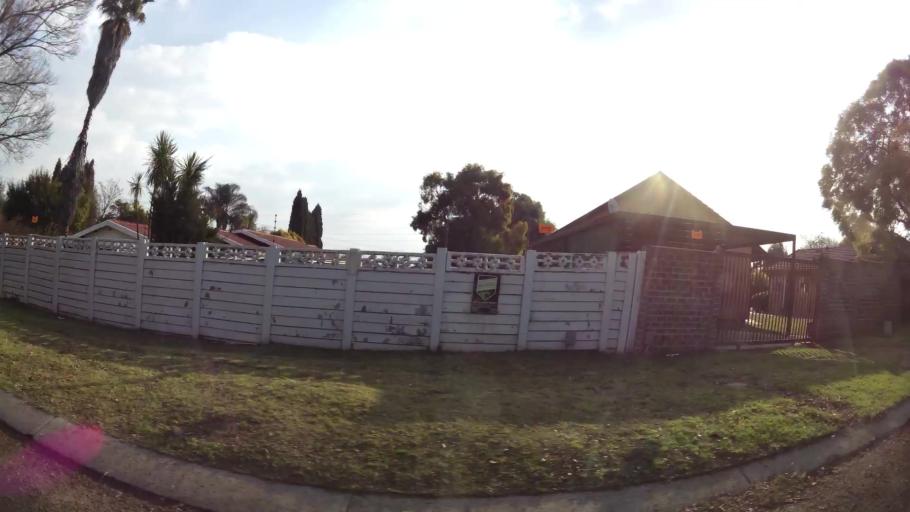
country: ZA
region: Gauteng
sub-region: City of Johannesburg Metropolitan Municipality
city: Modderfontein
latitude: -26.1323
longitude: 28.1936
